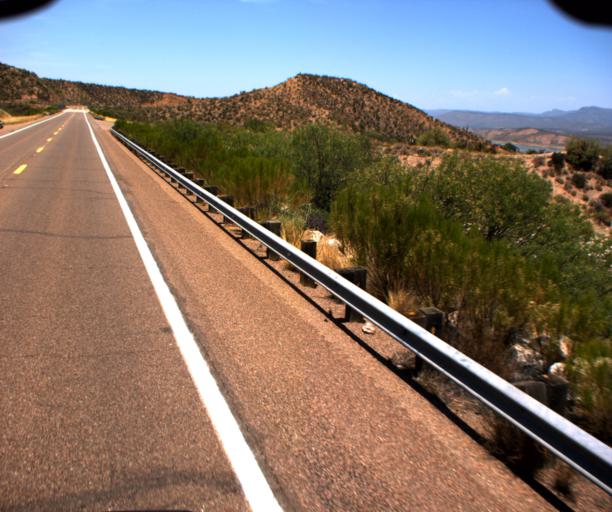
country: US
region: Arizona
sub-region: Gila County
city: Tonto Basin
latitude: 33.7118
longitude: -111.2005
